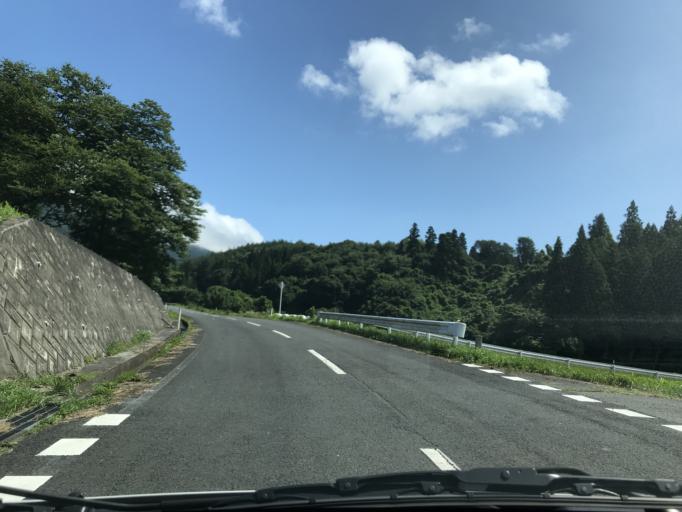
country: JP
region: Iwate
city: Ofunato
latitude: 39.0019
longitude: 141.4257
